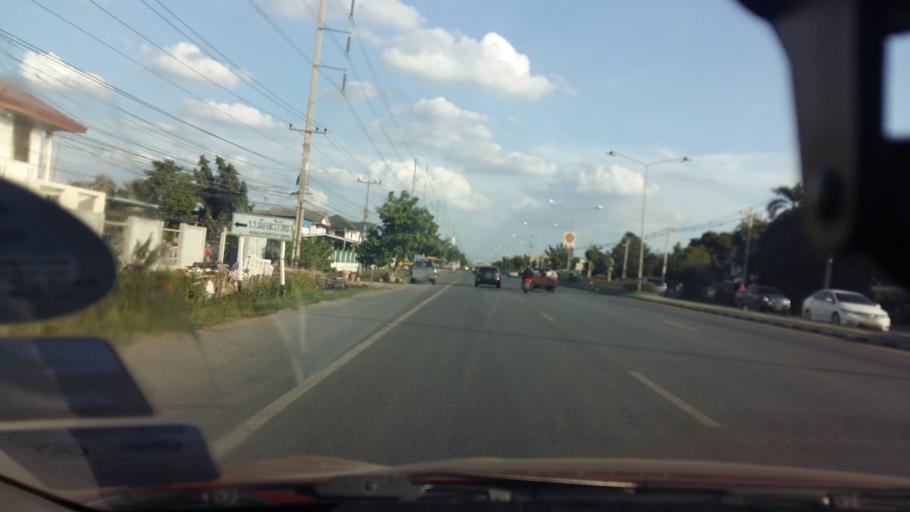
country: TH
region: Lop Buri
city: Lop Buri
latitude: 14.8336
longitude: 100.6457
